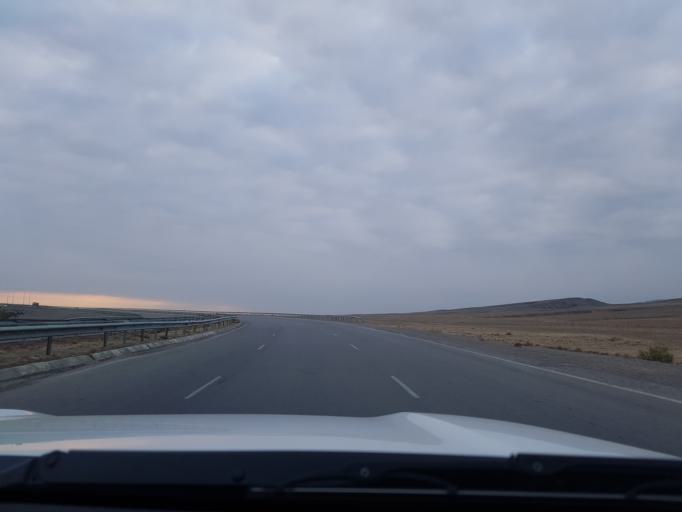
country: IR
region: Razavi Khorasan
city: Dargaz
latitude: 37.6826
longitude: 59.0728
